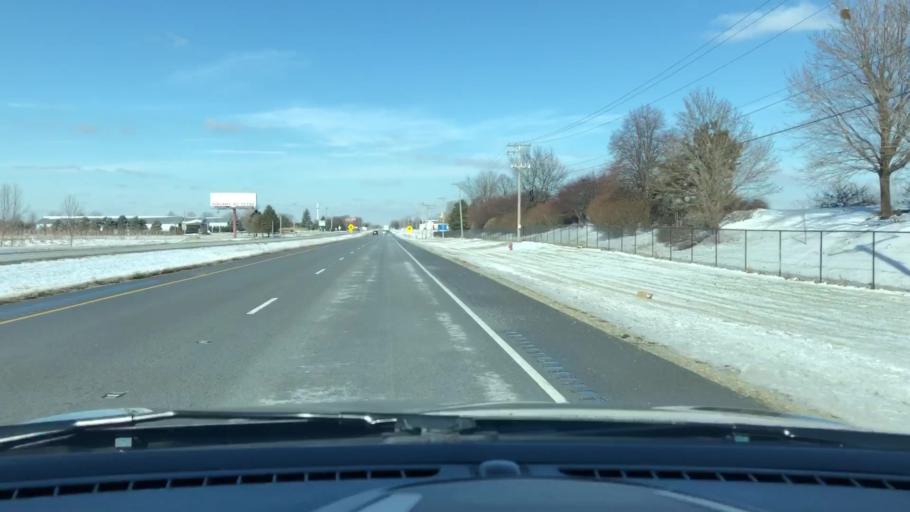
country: US
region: Illinois
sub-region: Will County
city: Preston Heights
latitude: 41.4633
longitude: -88.0794
